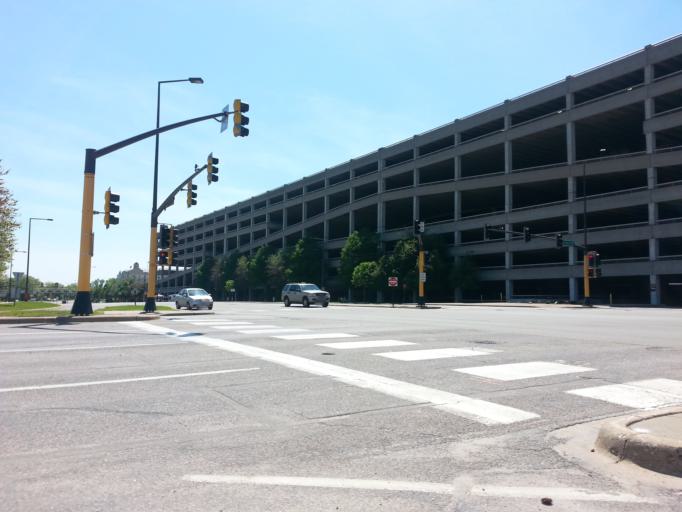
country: US
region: Minnesota
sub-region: Hennepin County
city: Richfield
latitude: 44.8553
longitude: -93.2373
